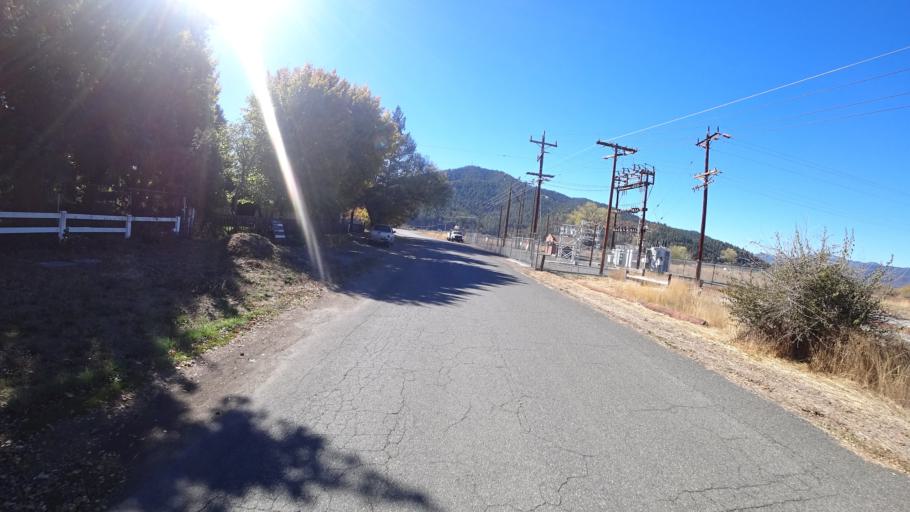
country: US
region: California
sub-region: Siskiyou County
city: Yreka
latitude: 41.6054
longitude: -122.8496
